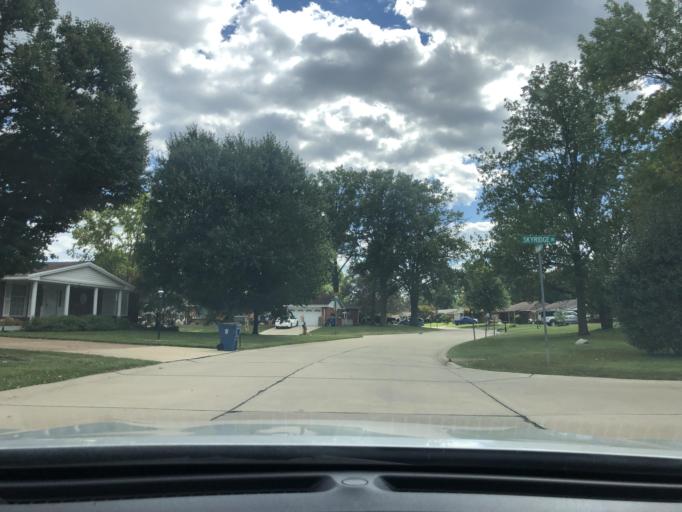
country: US
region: Missouri
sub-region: Saint Louis County
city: Concord
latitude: 38.4994
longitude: -90.3550
